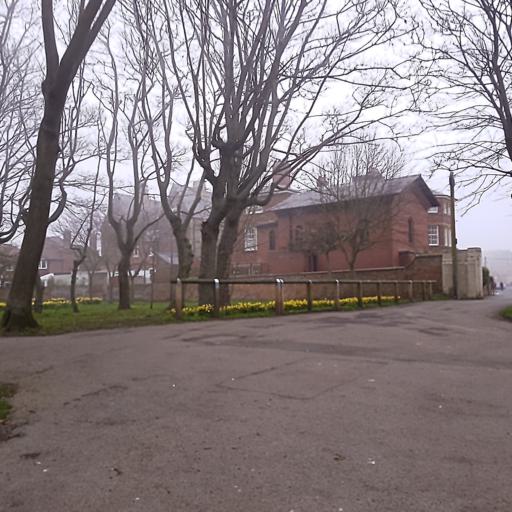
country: GB
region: England
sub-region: North Yorkshire
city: Filey
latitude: 54.2041
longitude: -0.2875
